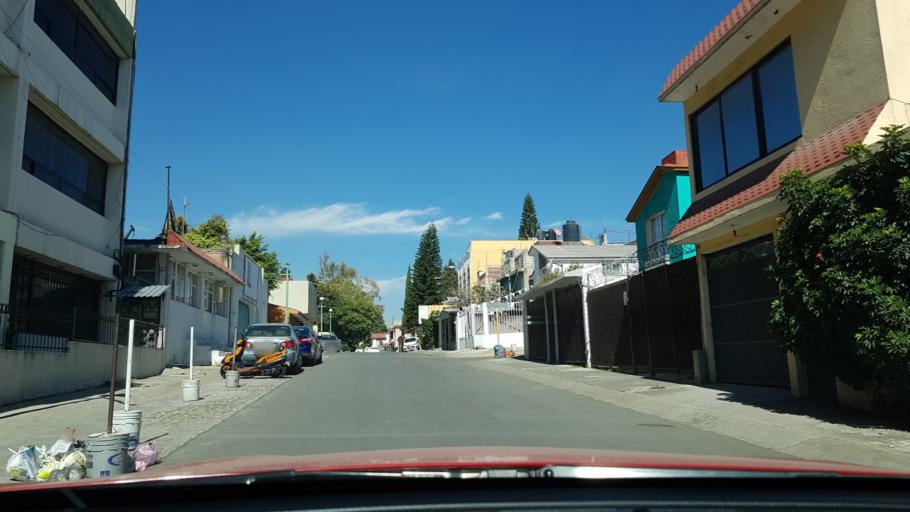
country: MX
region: Mexico
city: Cuautitlan Izcalli
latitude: 19.6390
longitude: -99.1977
